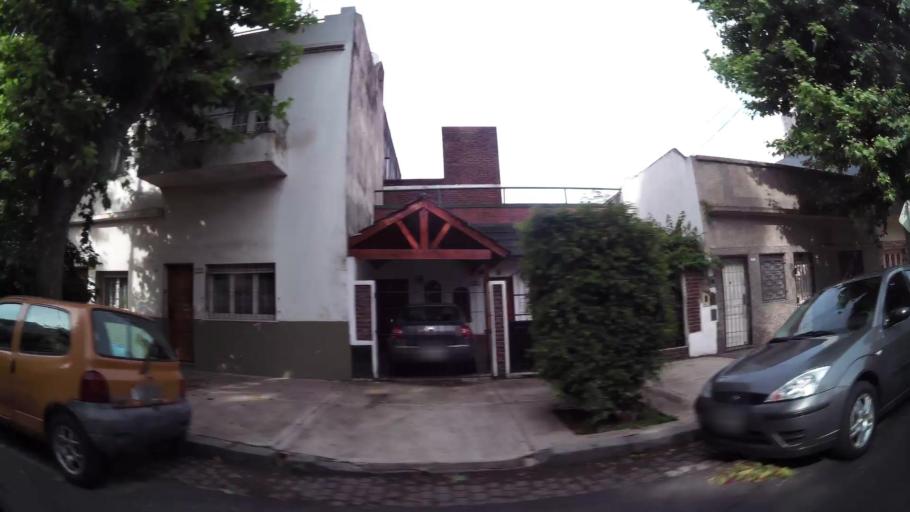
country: AR
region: Buenos Aires F.D.
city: Buenos Aires
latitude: -34.6441
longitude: -58.4209
